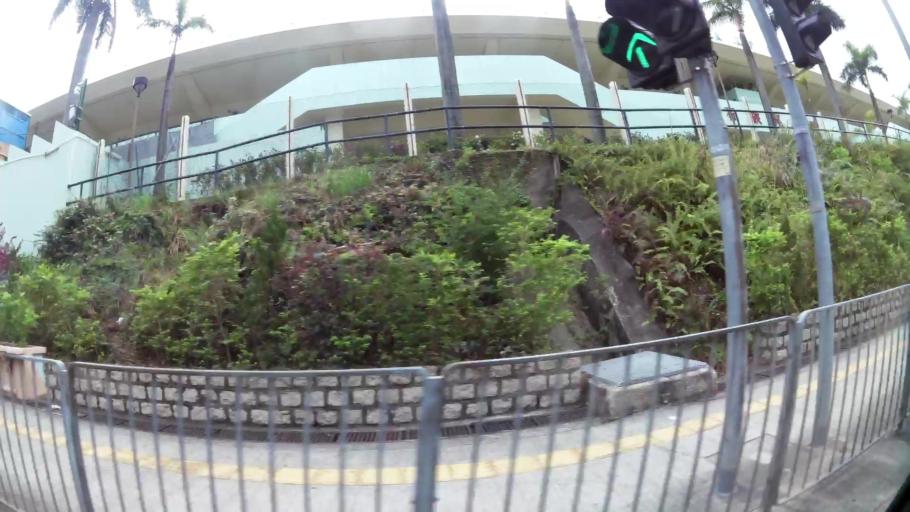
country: HK
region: Sham Shui Po
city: Sham Shui Po
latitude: 22.3364
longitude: 114.1692
